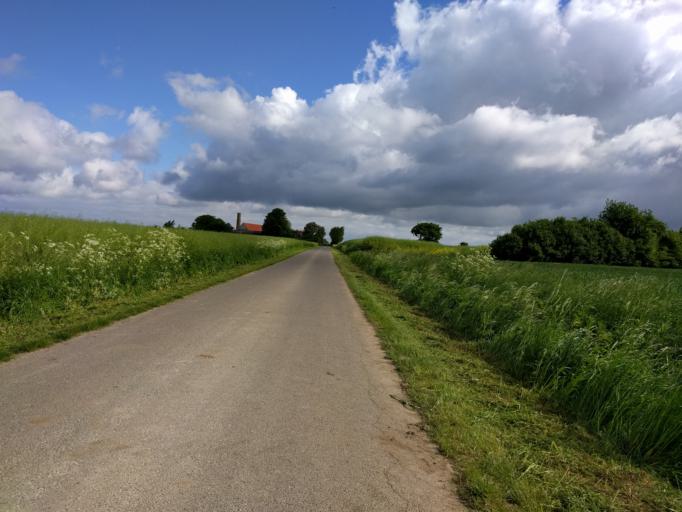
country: DK
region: South Denmark
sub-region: Kerteminde Kommune
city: Kerteminde
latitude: 55.4261
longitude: 10.6289
